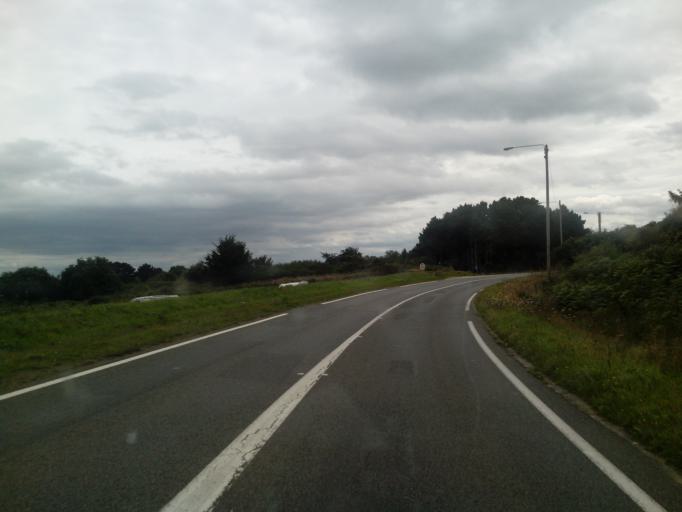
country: FR
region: Brittany
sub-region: Departement des Cotes-d'Armor
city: Etables-sur-Mer
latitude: 48.6319
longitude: -2.8232
